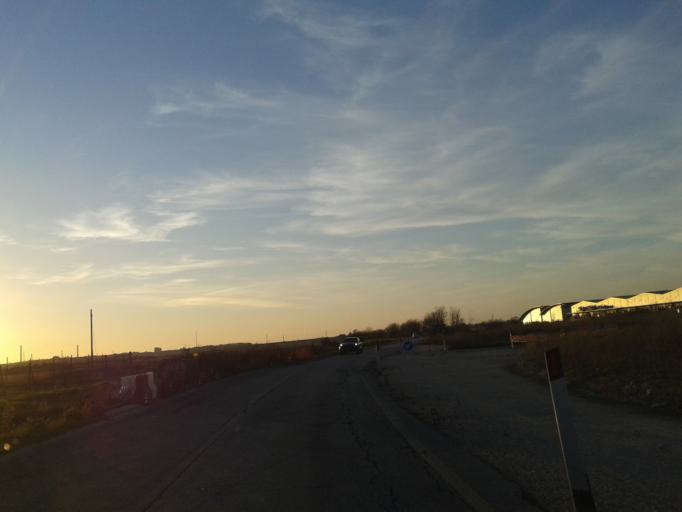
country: IT
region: Tuscany
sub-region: Provincia di Livorno
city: Guasticce
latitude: 43.5967
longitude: 10.3814
